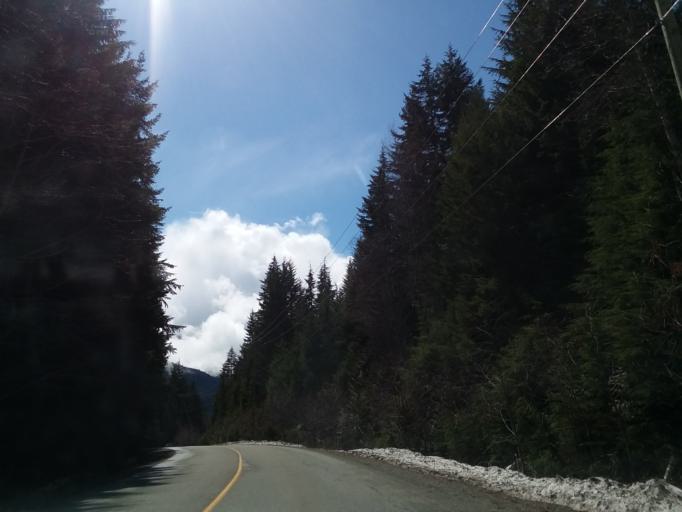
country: CA
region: British Columbia
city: Whistler
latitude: 50.1248
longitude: -122.9869
